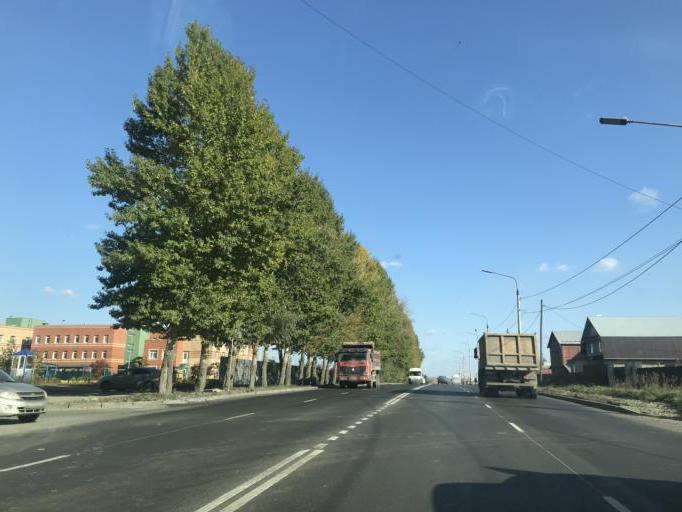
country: RU
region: Chelyabinsk
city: Roshchino
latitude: 55.2347
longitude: 61.3079
